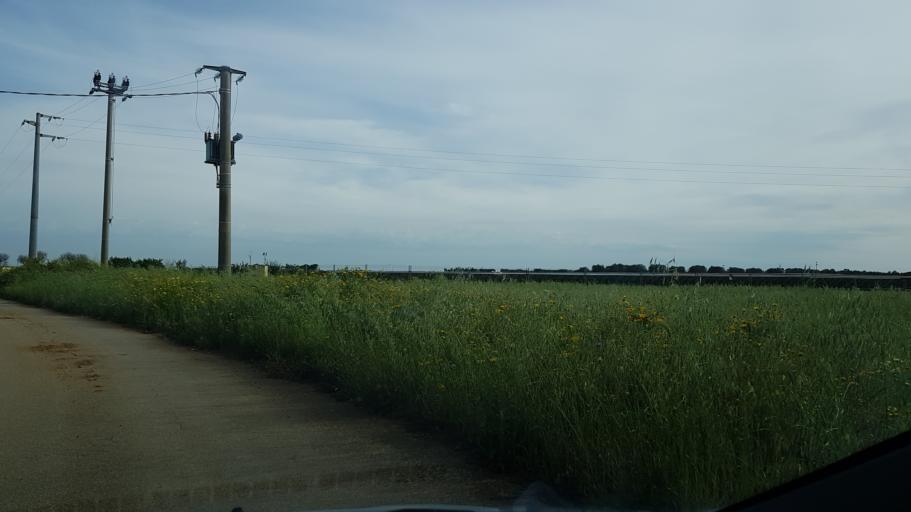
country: IT
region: Apulia
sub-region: Provincia di Brindisi
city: Tuturano
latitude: 40.5158
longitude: 17.9588
